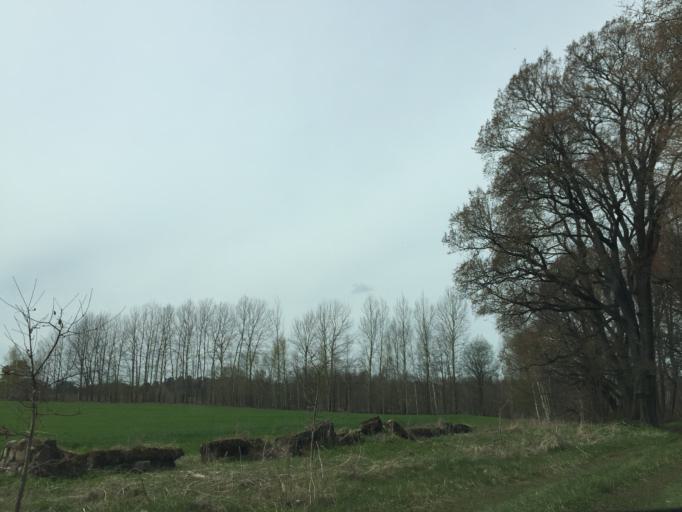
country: LV
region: Ludzas Rajons
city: Ludza
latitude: 56.5200
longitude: 27.5782
